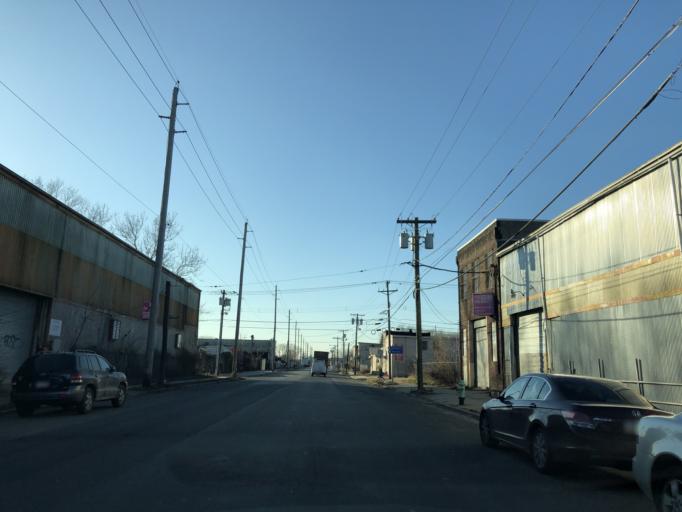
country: US
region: New Jersey
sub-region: Camden County
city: Camden
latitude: 39.9286
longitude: -75.1208
